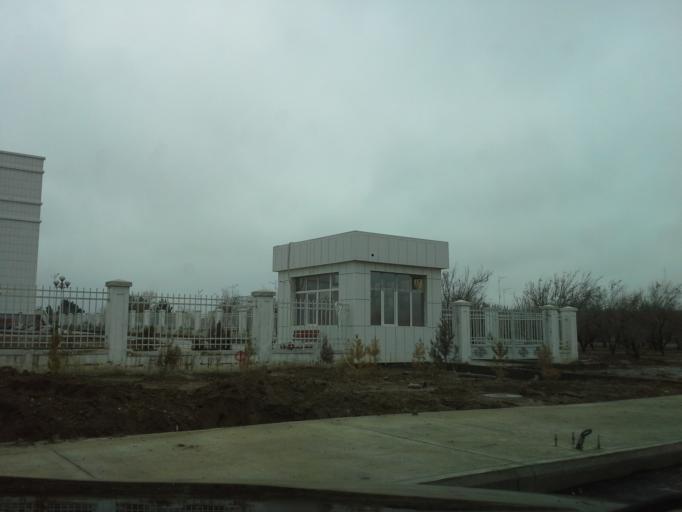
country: TM
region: Ahal
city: Ashgabat
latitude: 37.9756
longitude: 58.3994
